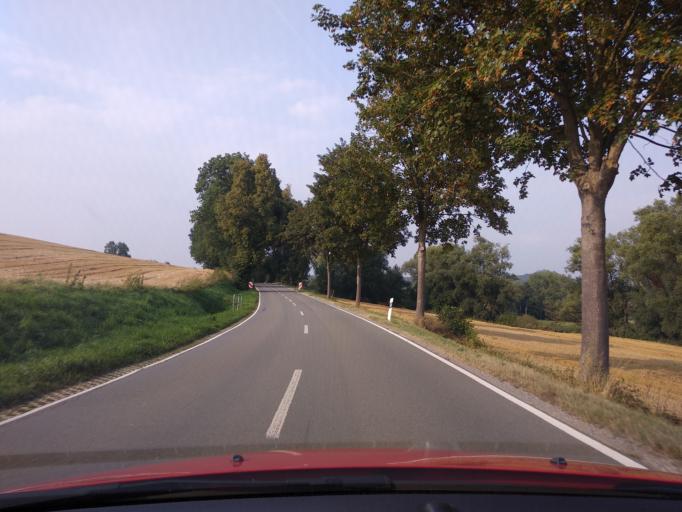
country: DE
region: Hesse
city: Liebenau
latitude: 51.4512
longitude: 9.3080
